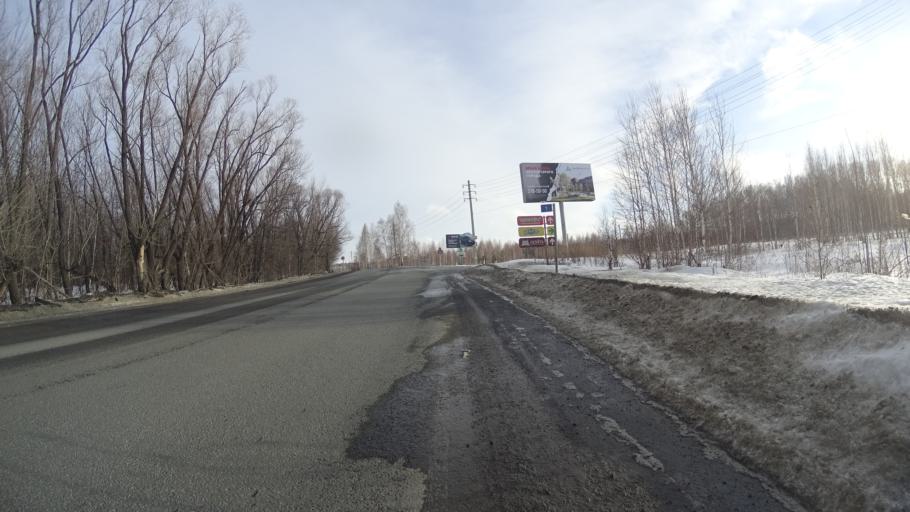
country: RU
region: Chelyabinsk
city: Sargazy
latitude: 55.1367
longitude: 61.2830
